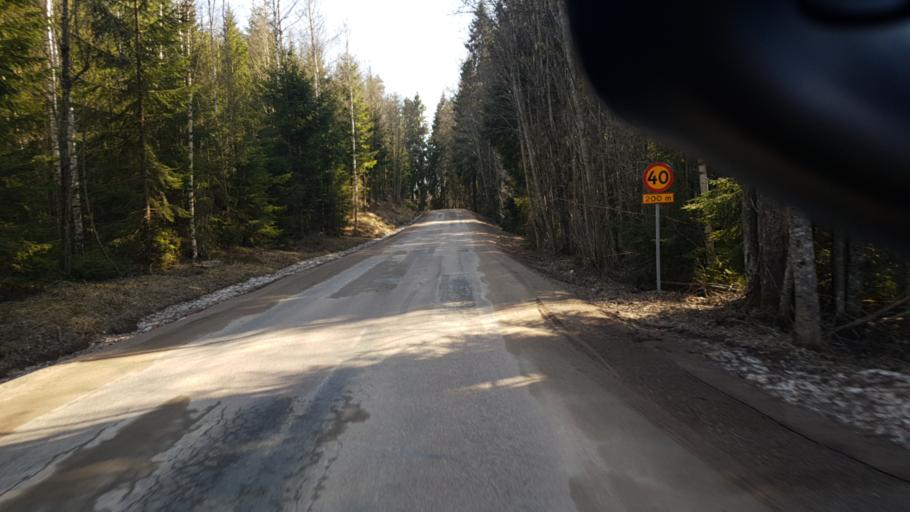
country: SE
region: Vaermland
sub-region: Arvika Kommun
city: Arvika
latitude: 59.6381
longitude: 12.8165
